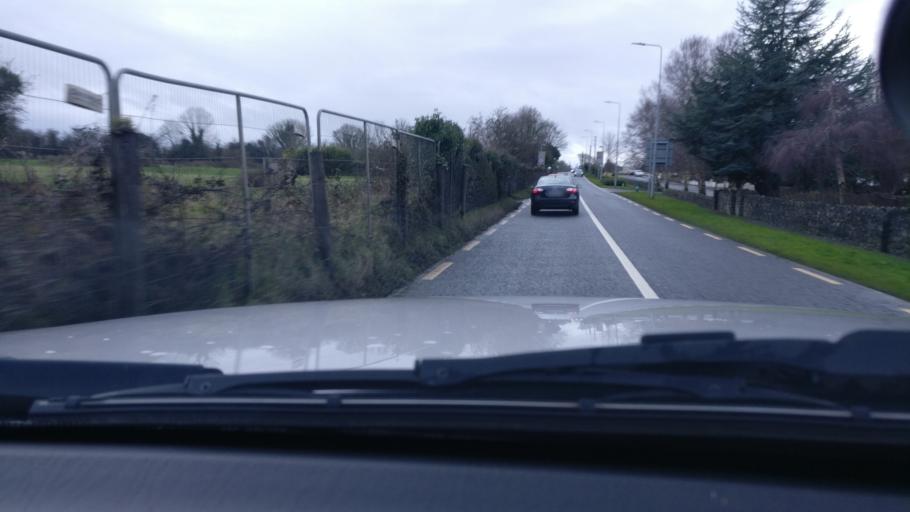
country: IE
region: Leinster
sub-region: An Iarmhi
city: Athlone
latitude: 53.4689
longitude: -7.8650
